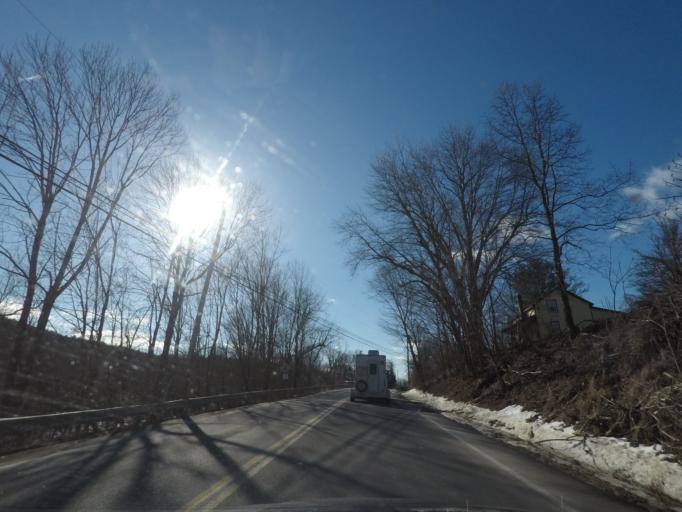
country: US
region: New York
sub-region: Columbia County
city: Chatham
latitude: 42.4203
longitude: -73.5004
